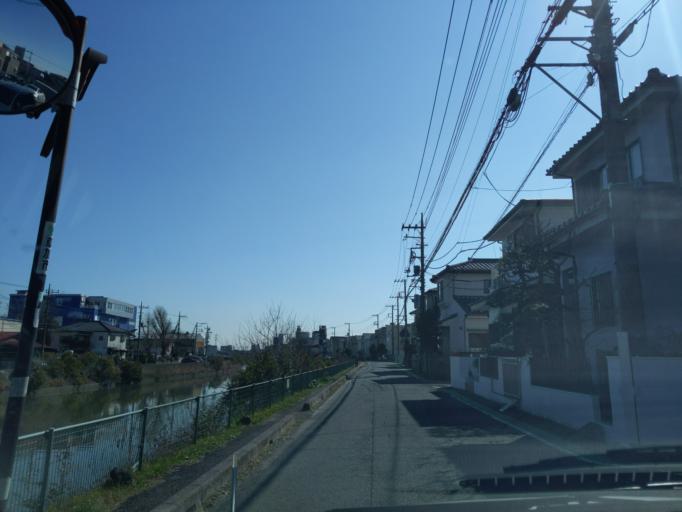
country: JP
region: Saitama
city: Soka
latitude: 35.8331
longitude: 139.8101
